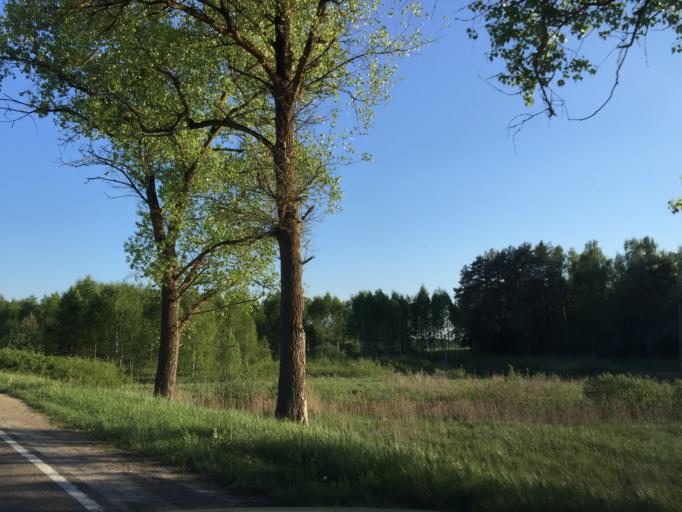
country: LV
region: Kekava
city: Kekava
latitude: 56.7782
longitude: 24.3008
